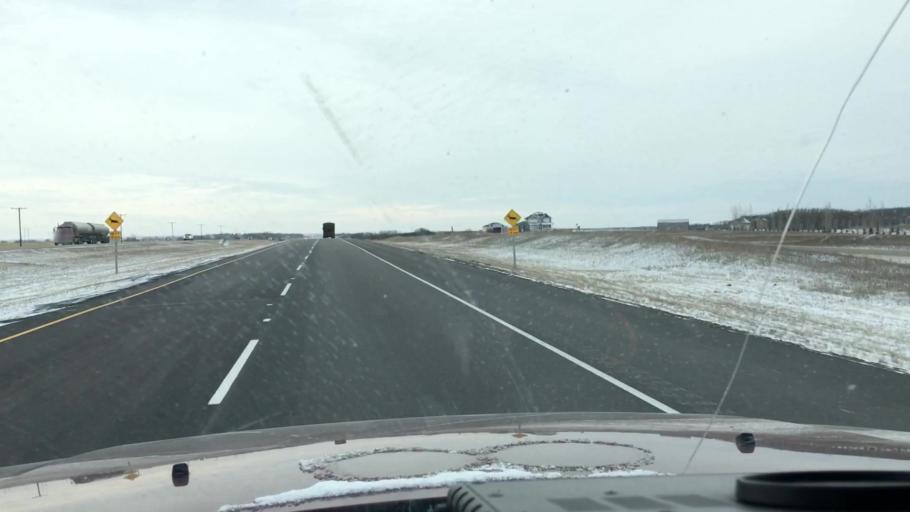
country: CA
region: Saskatchewan
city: Saskatoon
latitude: 51.9309
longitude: -106.5358
